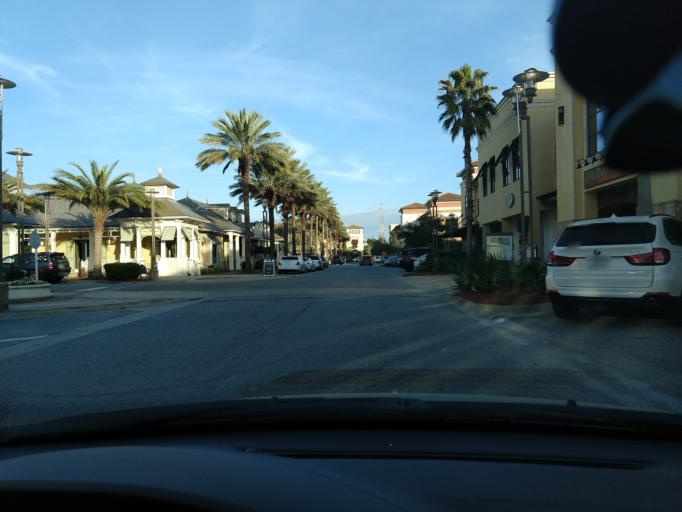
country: US
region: Florida
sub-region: Walton County
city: Miramar Beach
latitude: 30.3791
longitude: -86.3148
